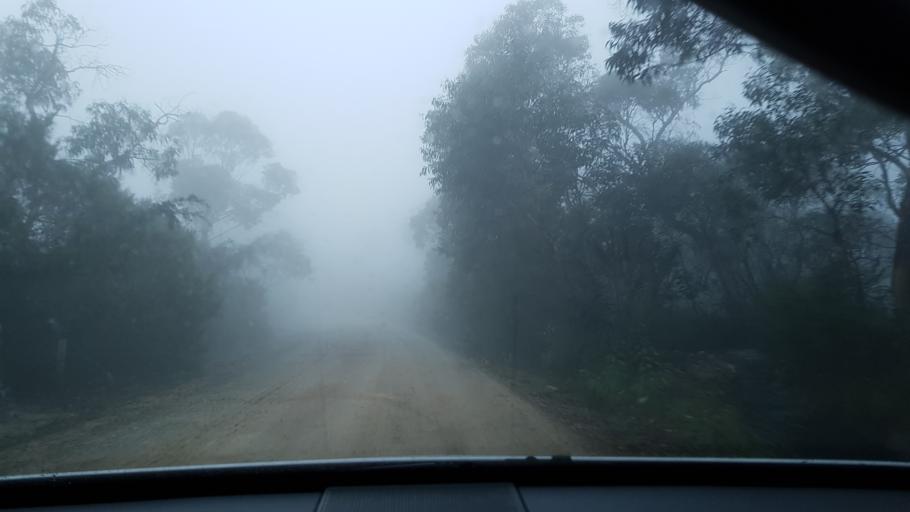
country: AU
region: New South Wales
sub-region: Blue Mountains Municipality
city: Katoomba
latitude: -33.9946
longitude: 150.0965
